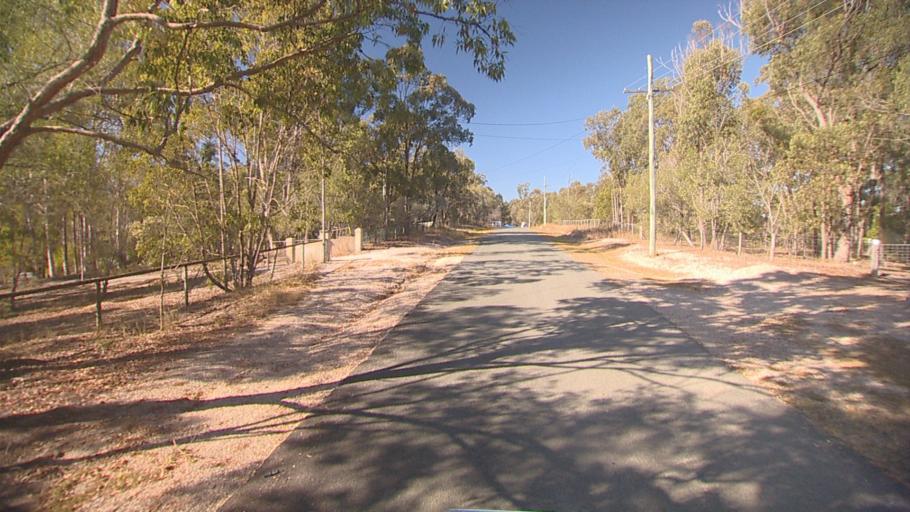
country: AU
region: Queensland
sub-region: Logan
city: Chambers Flat
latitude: -27.7929
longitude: 153.1331
